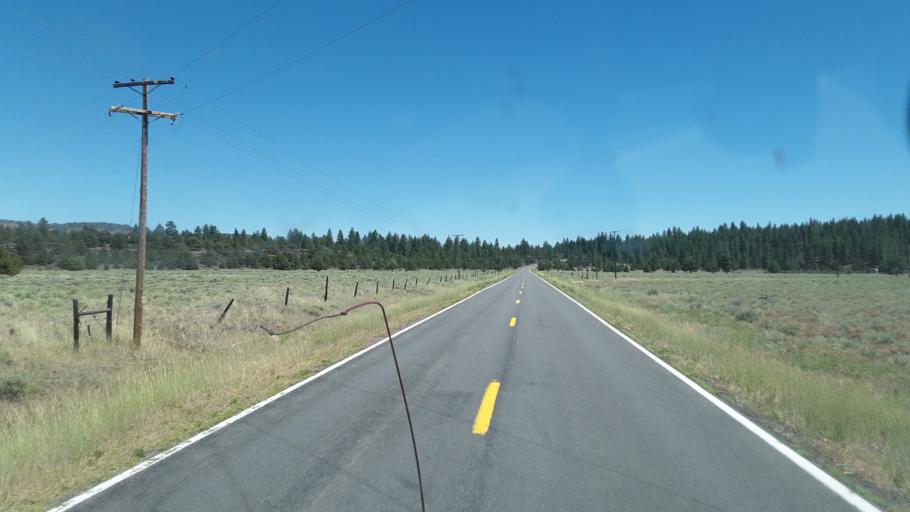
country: US
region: California
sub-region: Lassen County
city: Susanville
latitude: 40.5192
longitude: -120.5845
